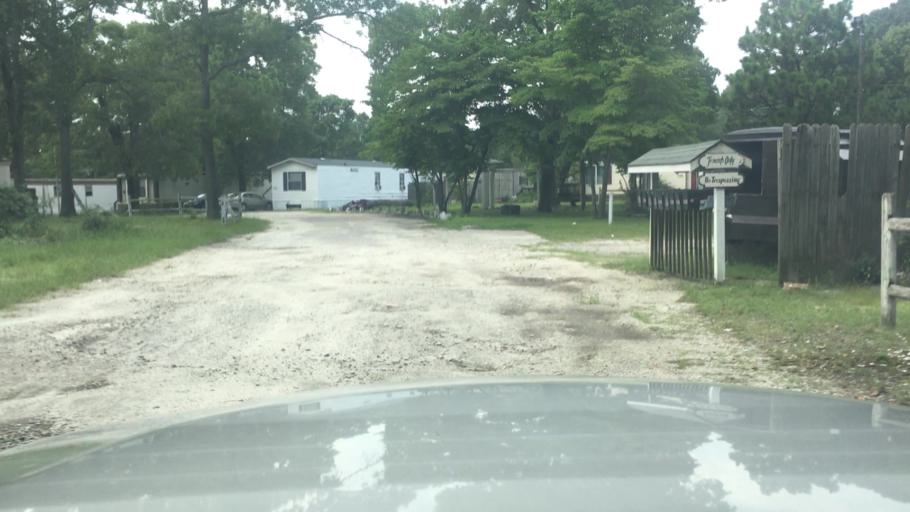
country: US
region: North Carolina
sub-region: Cumberland County
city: Spring Lake
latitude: 35.1510
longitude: -78.9160
